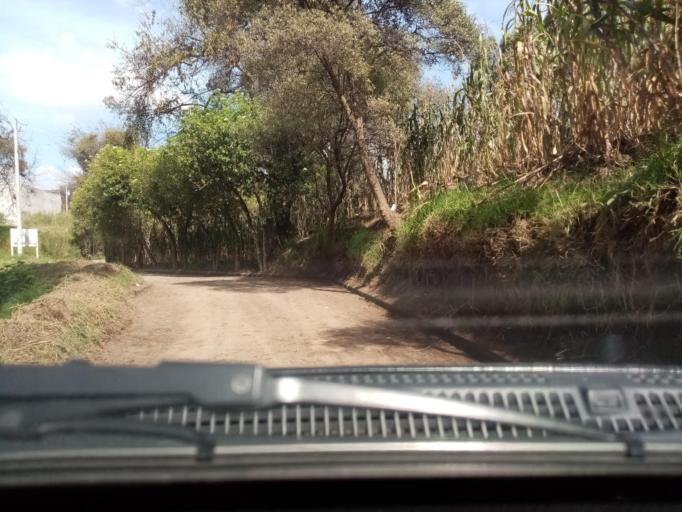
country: GT
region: Quetzaltenango
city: Quetzaltenango
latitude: 14.8580
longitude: -91.5306
